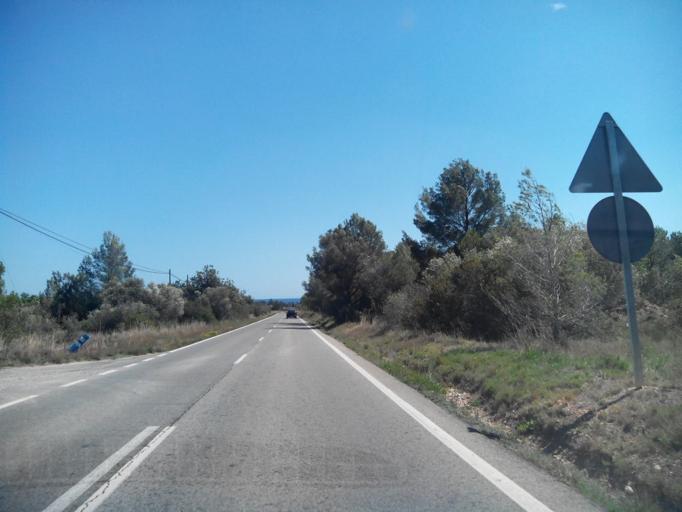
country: ES
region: Catalonia
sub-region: Provincia de Tarragona
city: Riudecanyes
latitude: 41.0675
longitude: 0.9838
